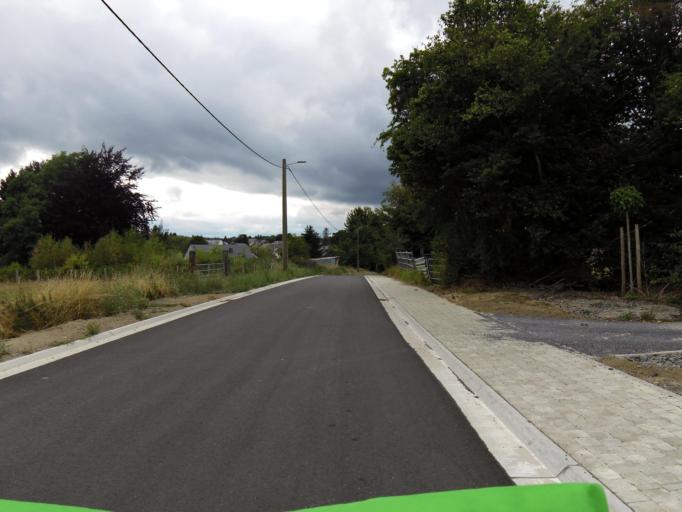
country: BE
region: Wallonia
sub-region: Province de Namur
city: Bievre
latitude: 49.9385
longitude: 5.0186
